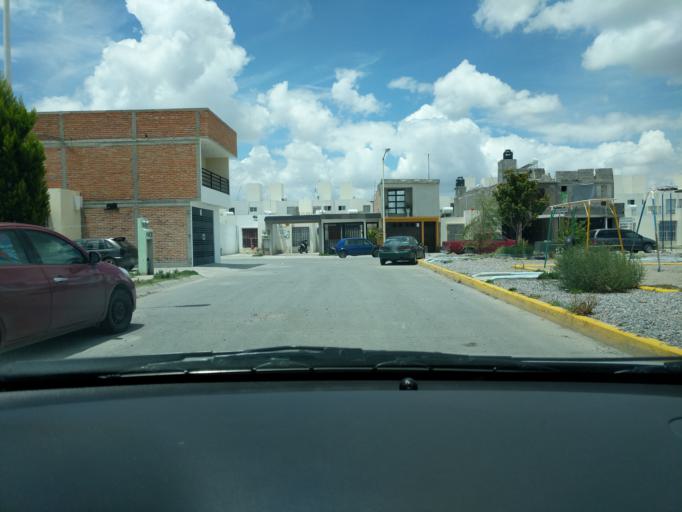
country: MX
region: San Luis Potosi
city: Soledad Diez Gutierrez
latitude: 22.2177
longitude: -100.9340
